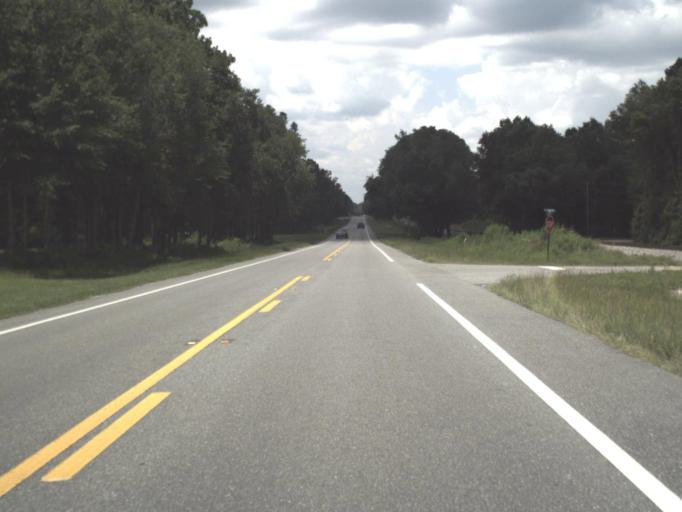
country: US
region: Florida
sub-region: Columbia County
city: Five Points
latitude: 30.2730
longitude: -82.6942
